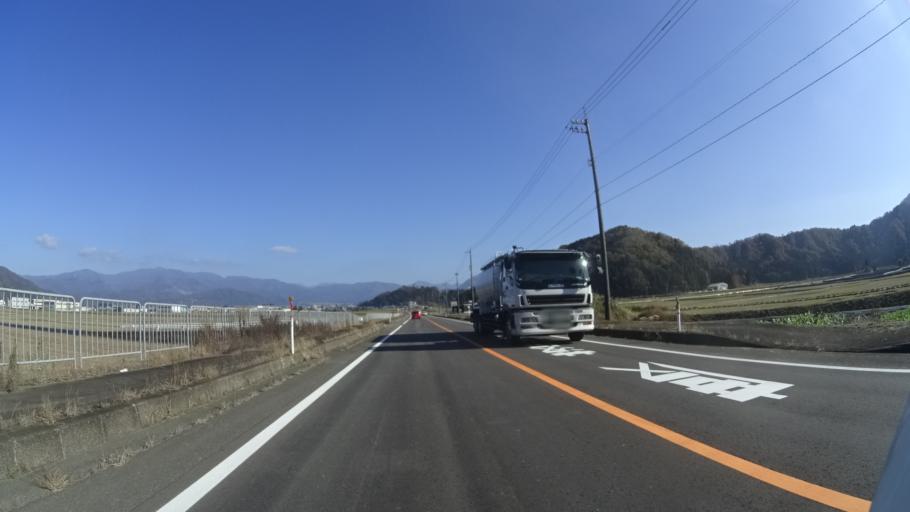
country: JP
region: Fukui
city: Ono
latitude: 35.9896
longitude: 136.4635
